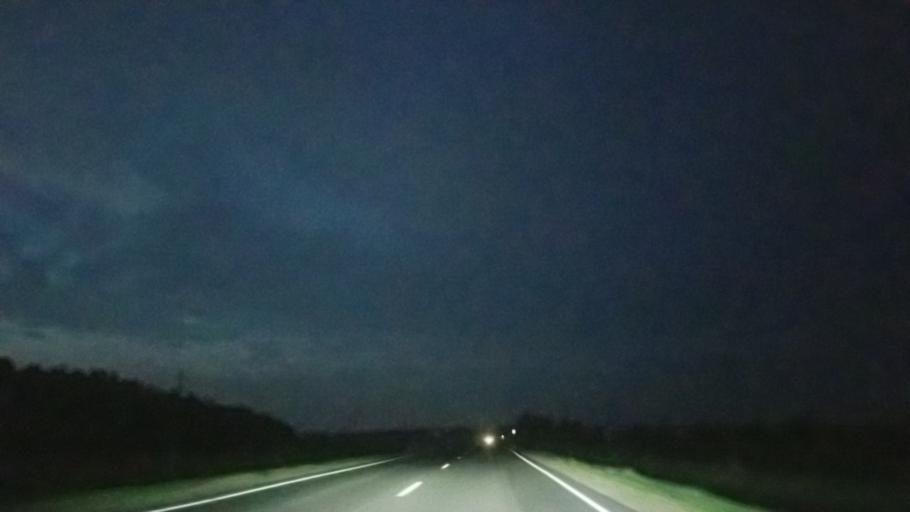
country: BY
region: Brest
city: Brest
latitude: 51.9992
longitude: 23.7131
